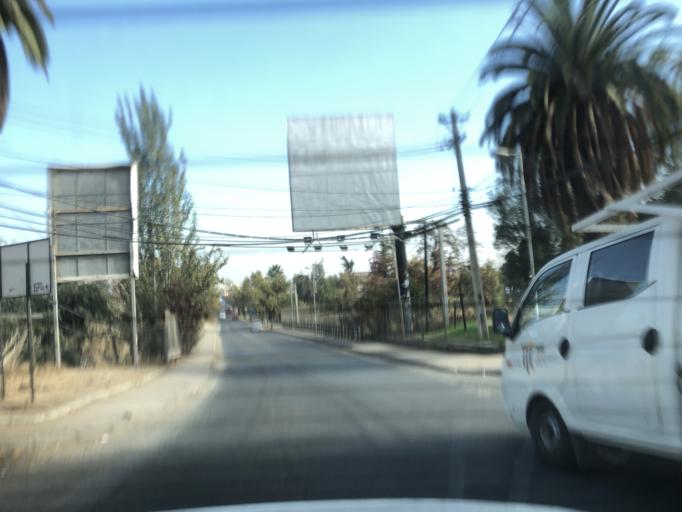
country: CL
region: Santiago Metropolitan
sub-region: Provincia de Cordillera
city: Puente Alto
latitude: -33.5710
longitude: -70.5517
